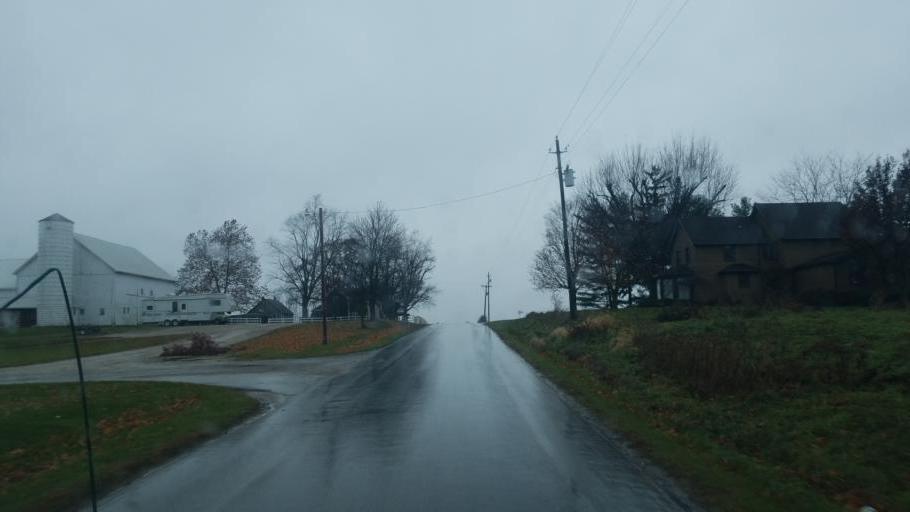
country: US
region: Indiana
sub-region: Adams County
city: Geneva
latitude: 40.6149
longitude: -84.9183
